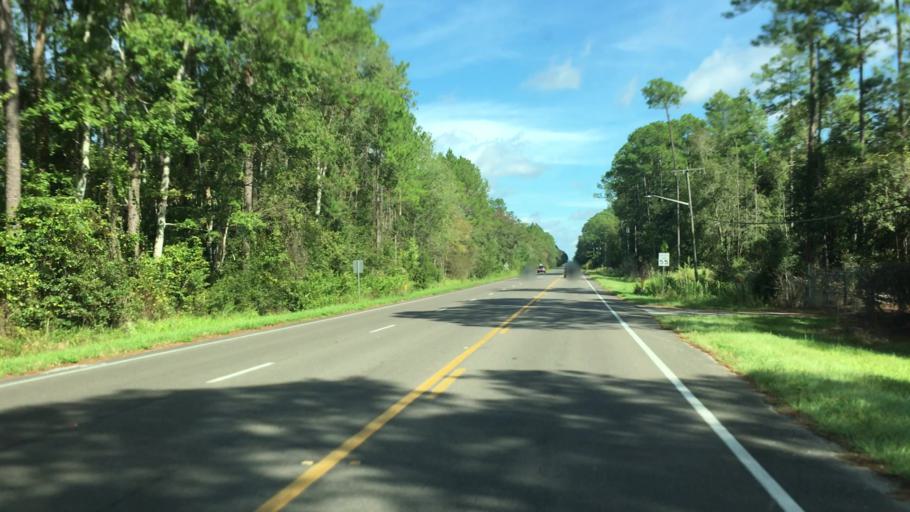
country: US
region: Florida
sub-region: Alachua County
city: Gainesville
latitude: 29.7064
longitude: -82.2774
